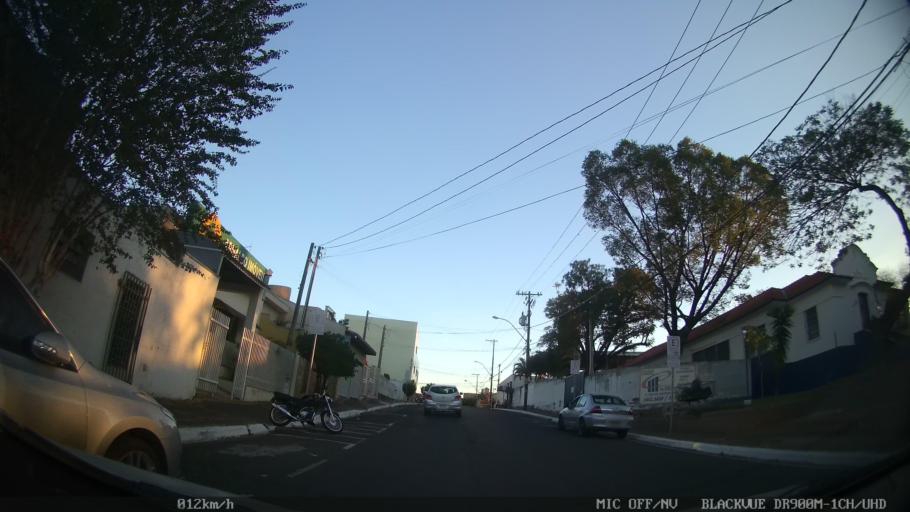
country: BR
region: Sao Paulo
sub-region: Santa Barbara D'Oeste
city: Santa Barbara d'Oeste
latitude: -22.7561
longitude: -47.4165
